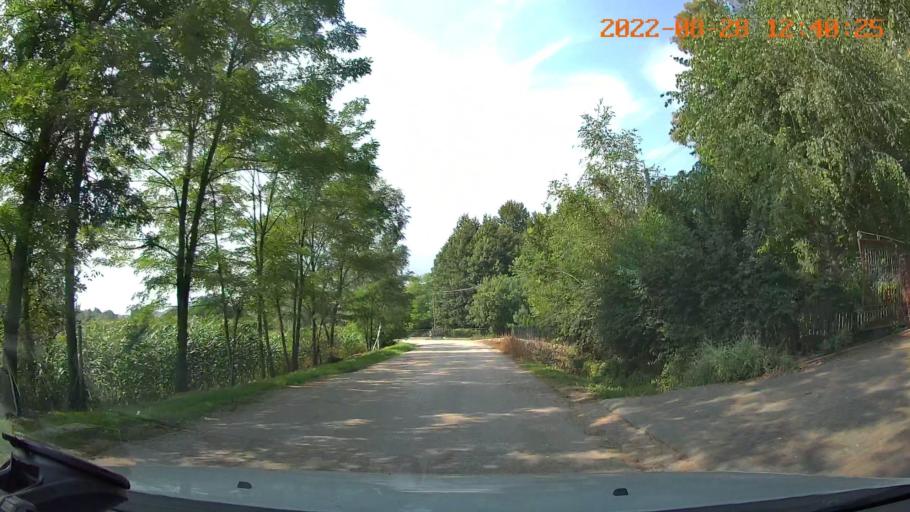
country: PL
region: Swietokrzyskie
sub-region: Powiat pinczowski
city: Dzialoszyce
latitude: 50.3716
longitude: 20.3648
